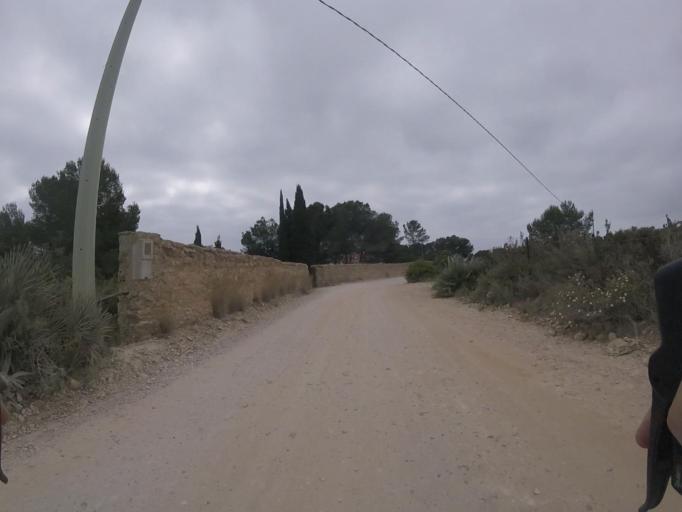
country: ES
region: Valencia
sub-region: Provincia de Castello
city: Peniscola
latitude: 40.3335
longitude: 0.3739
